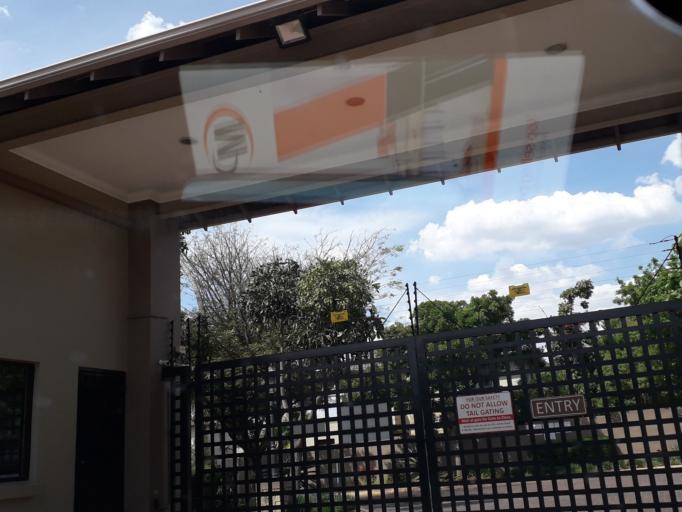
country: ZA
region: Gauteng
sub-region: City of Johannesburg Metropolitan Municipality
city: Roodepoort
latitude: -26.0979
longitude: 27.9068
